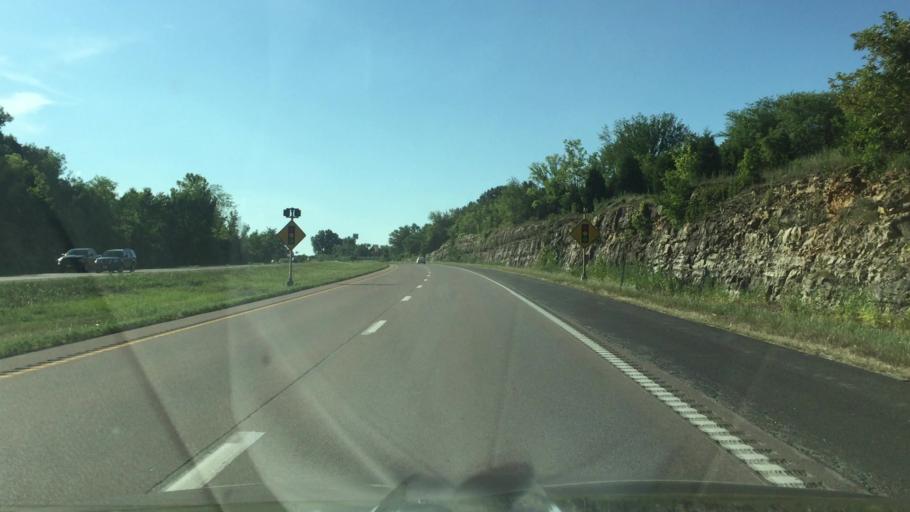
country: US
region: Missouri
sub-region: Pettis County
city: Sedalia
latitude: 38.7315
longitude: -93.3073
